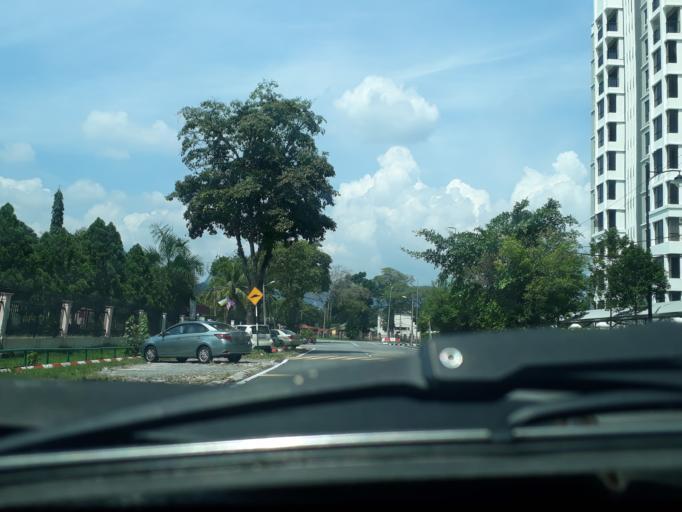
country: MY
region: Perak
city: Ipoh
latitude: 4.5945
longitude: 101.1151
